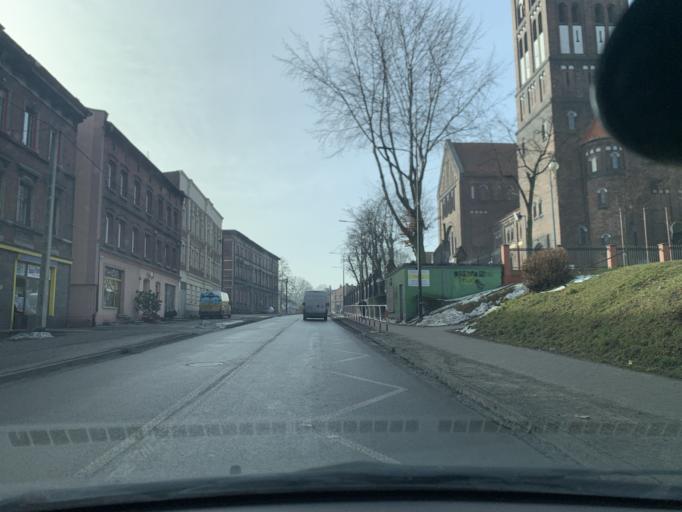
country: PL
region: Silesian Voivodeship
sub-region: Ruda Slaska
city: Ruda Slaska
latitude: 50.3203
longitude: 18.8569
